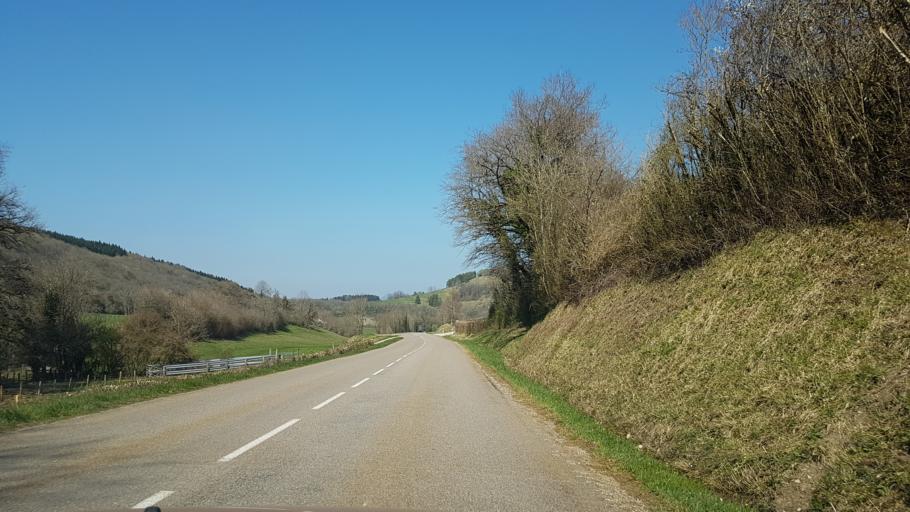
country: FR
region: Franche-Comte
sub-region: Departement du Jura
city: Orgelet
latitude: 46.5525
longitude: 5.6556
